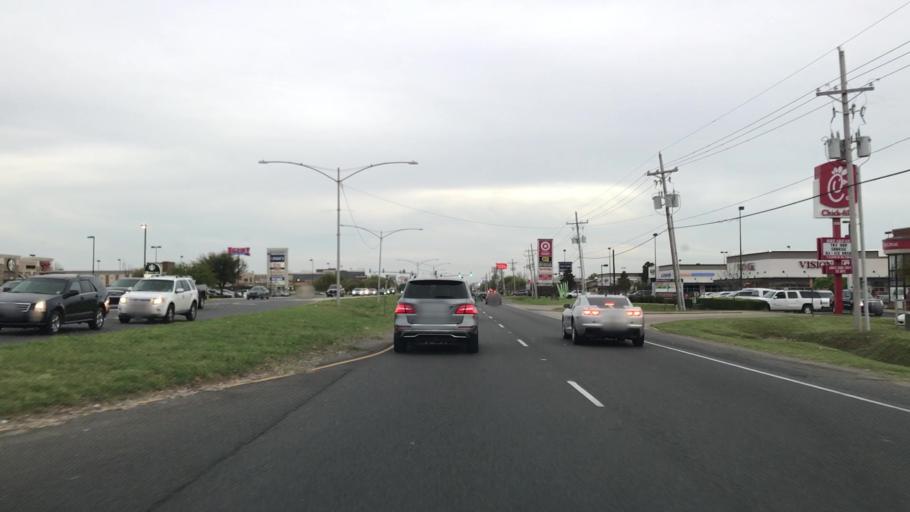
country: US
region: Louisiana
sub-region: Bossier Parish
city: Bossier City
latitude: 32.4432
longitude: -93.7186
